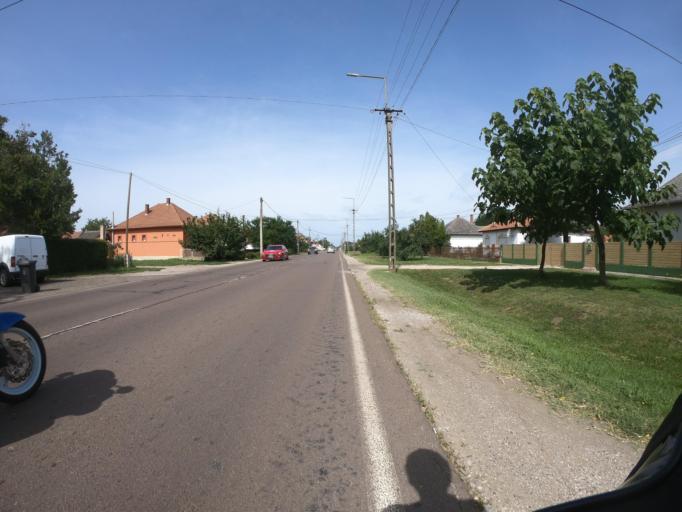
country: HU
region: Jasz-Nagykun-Szolnok
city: Tiszafured
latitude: 47.6054
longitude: 20.7759
